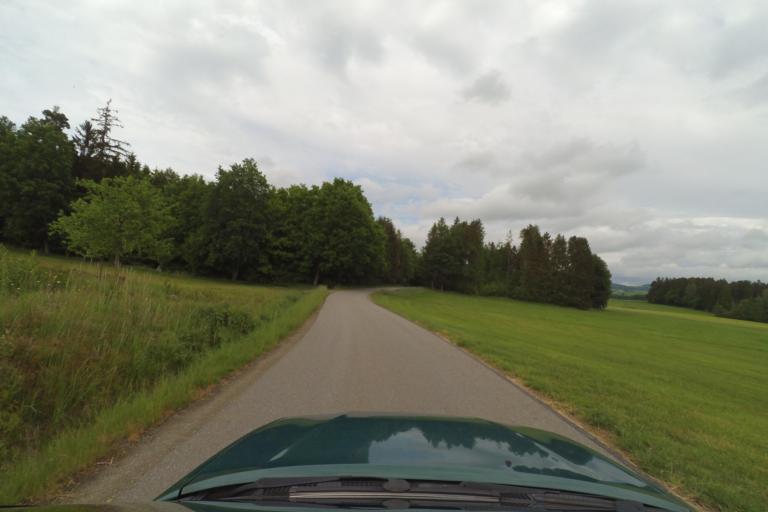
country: DE
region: Bavaria
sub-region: Upper Palatinate
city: Floss
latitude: 49.6828
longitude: 12.2848
